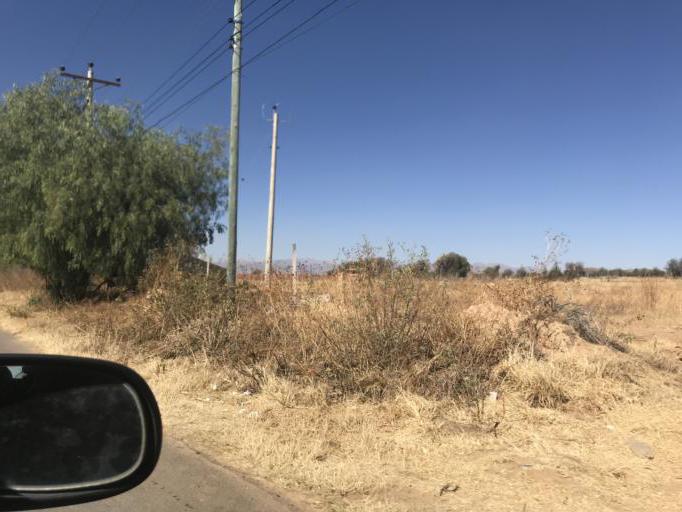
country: BO
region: Cochabamba
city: Tarata
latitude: -17.6075
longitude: -66.0006
